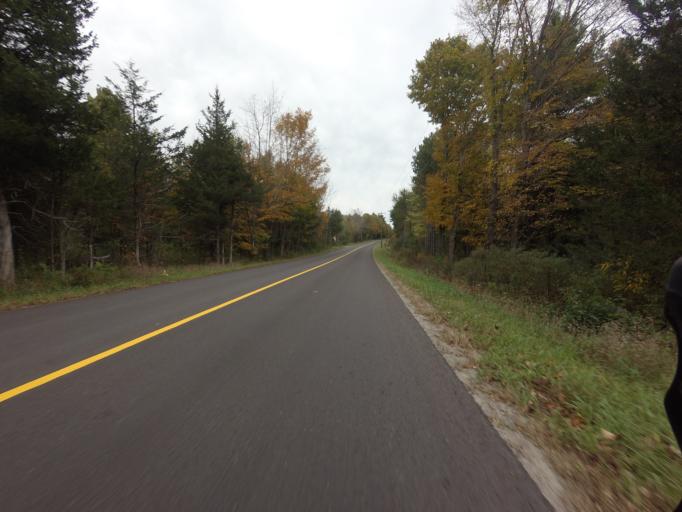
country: CA
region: Ontario
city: Gananoque
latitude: 44.5799
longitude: -76.0798
